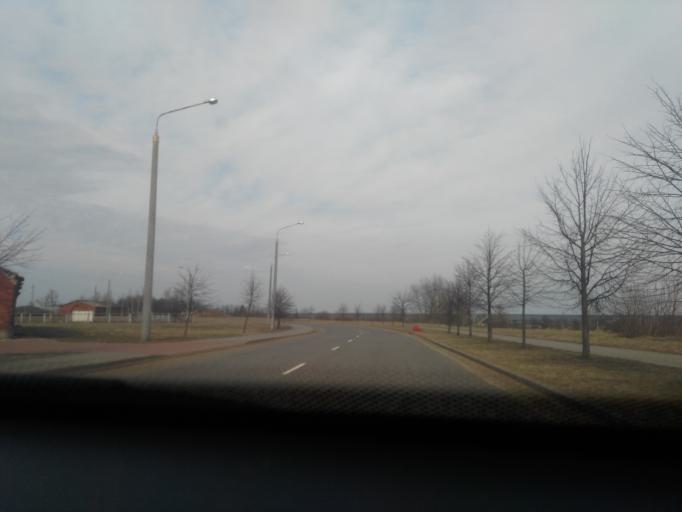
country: BY
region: Mogilev
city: Babruysk
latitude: 53.1418
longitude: 29.2505
